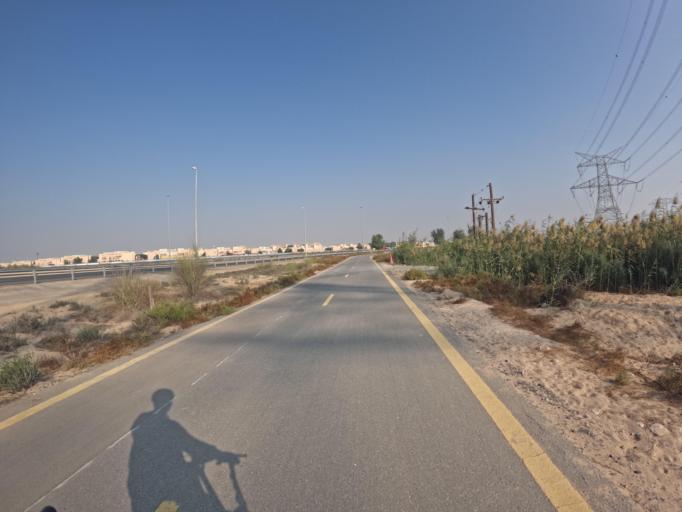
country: AE
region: Dubai
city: Dubai
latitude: 25.0228
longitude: 55.2837
